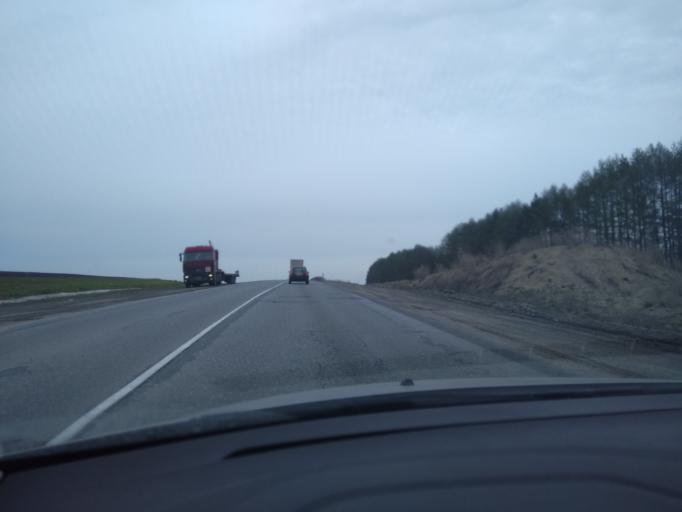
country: RU
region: Sverdlovsk
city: Kamyshlov
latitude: 56.8624
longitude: 62.9017
